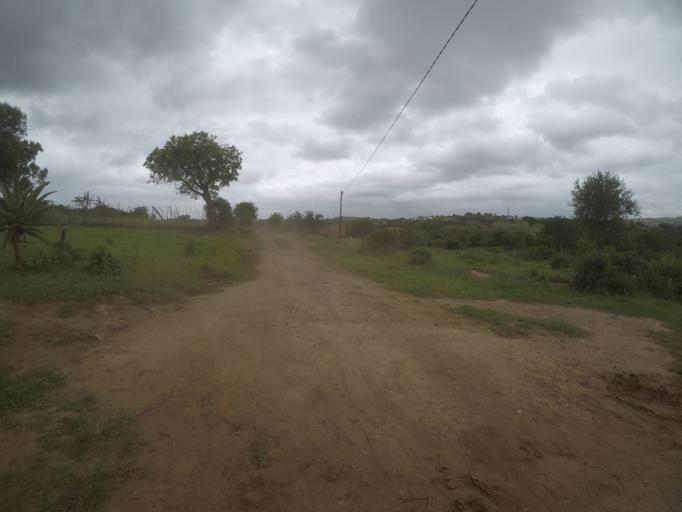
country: ZA
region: KwaZulu-Natal
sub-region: uThungulu District Municipality
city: Empangeni
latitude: -28.5923
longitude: 31.8433
